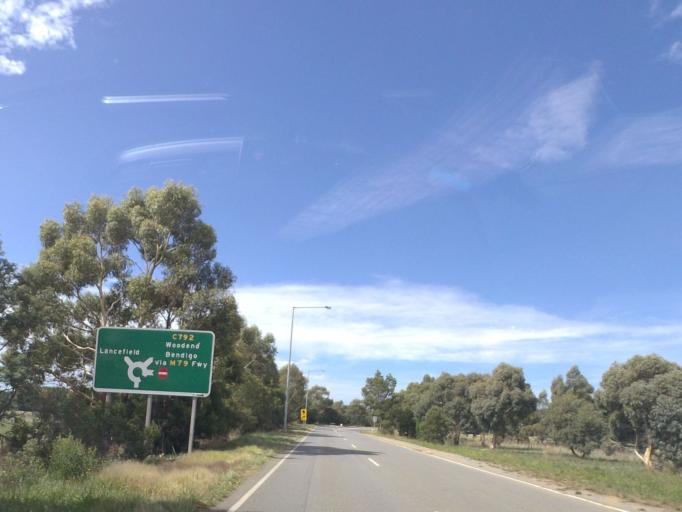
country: AU
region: Victoria
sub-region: Hume
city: Sunbury
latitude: -37.3183
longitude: 144.5257
